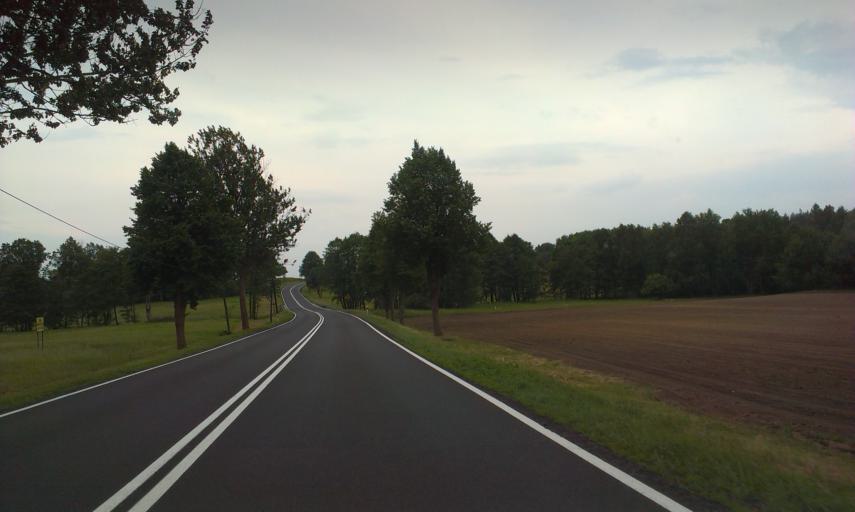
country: PL
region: West Pomeranian Voivodeship
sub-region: Powiat szczecinecki
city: Szczecinek
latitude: 53.8116
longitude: 16.6433
